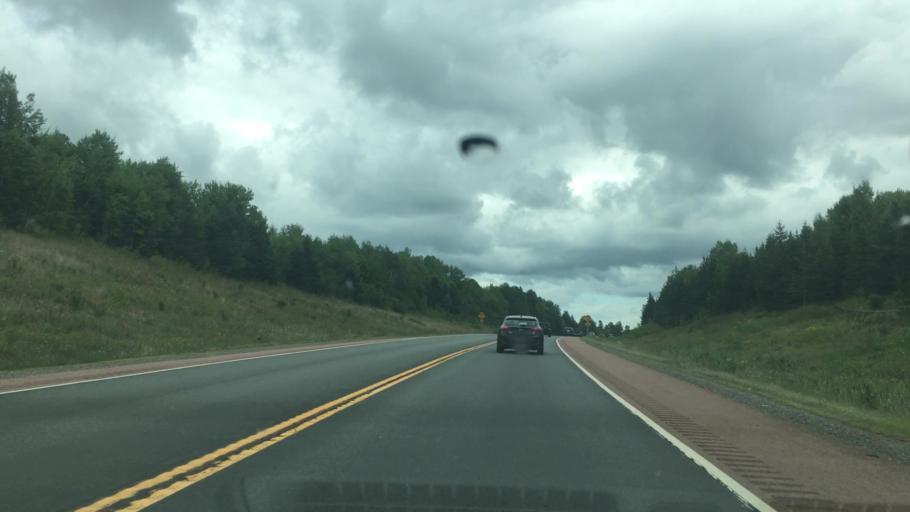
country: CA
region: Nova Scotia
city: Antigonish
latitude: 45.5958
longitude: -62.0557
